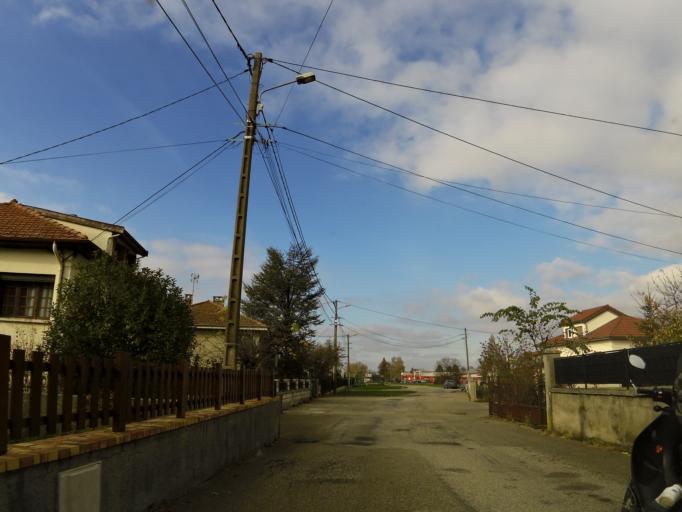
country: FR
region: Rhone-Alpes
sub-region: Departement de l'Ain
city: Amberieu-en-Bugey
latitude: 45.9601
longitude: 5.3461
